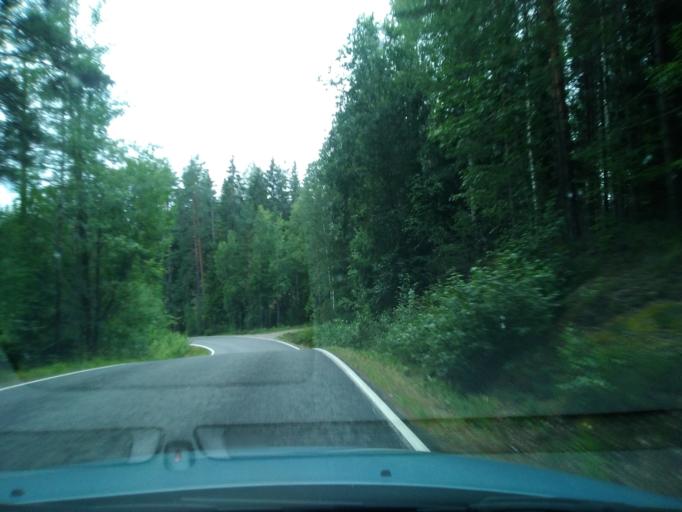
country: FI
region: Uusimaa
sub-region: Helsinki
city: Kaerkoelae
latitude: 60.7780
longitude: 24.0731
